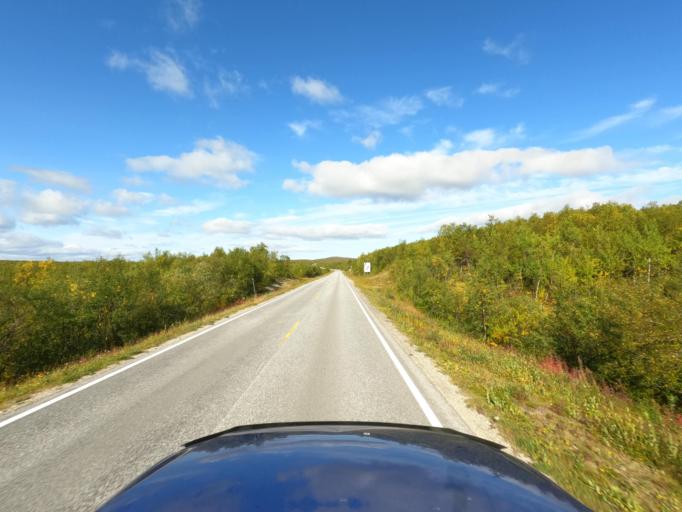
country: NO
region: Finnmark Fylke
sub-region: Karasjok
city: Karasjohka
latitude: 69.5375
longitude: 25.4318
